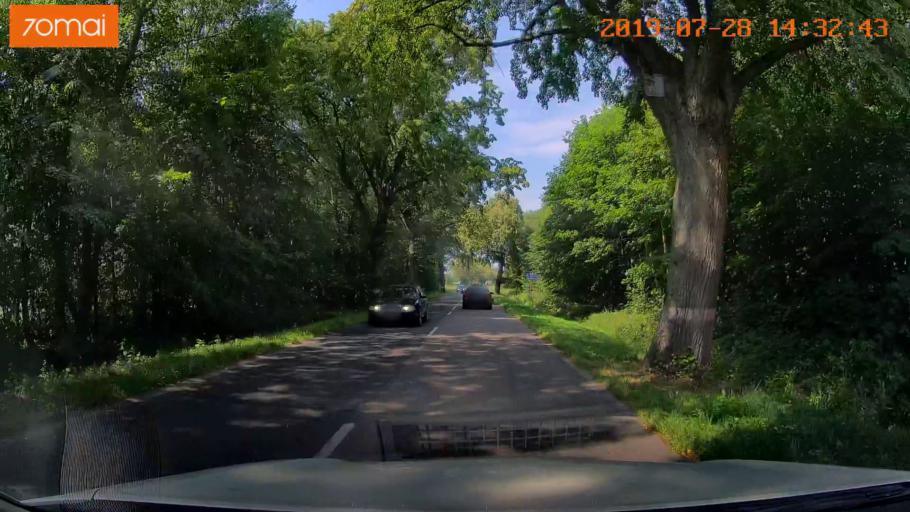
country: RU
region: Kaliningrad
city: Primorsk
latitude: 54.8146
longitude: 20.0386
